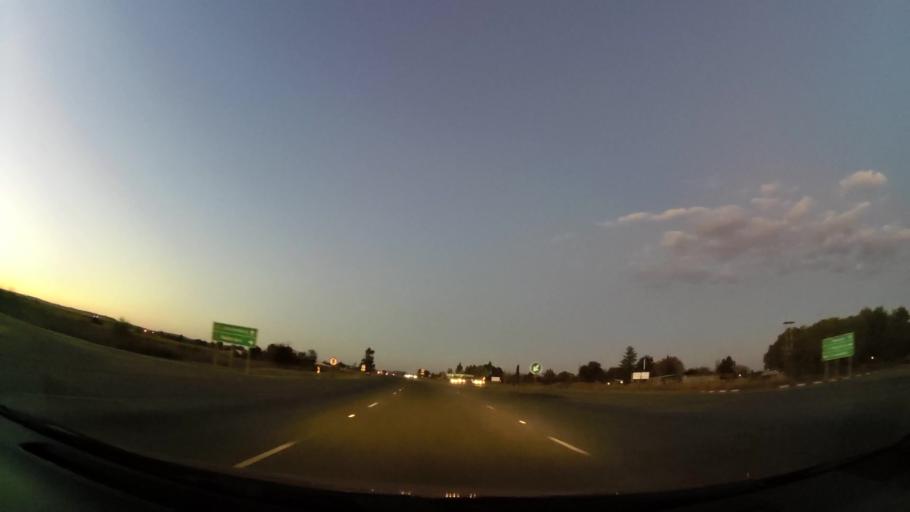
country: ZA
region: North-West
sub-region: Dr Kenneth Kaunda District Municipality
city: Potchefstroom
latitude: -26.7045
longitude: 27.1249
